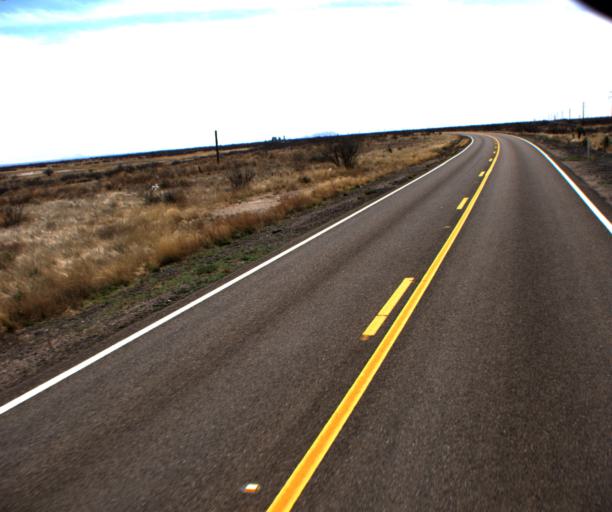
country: US
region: Arizona
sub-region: Cochise County
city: Willcox
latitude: 32.1465
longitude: -109.9342
